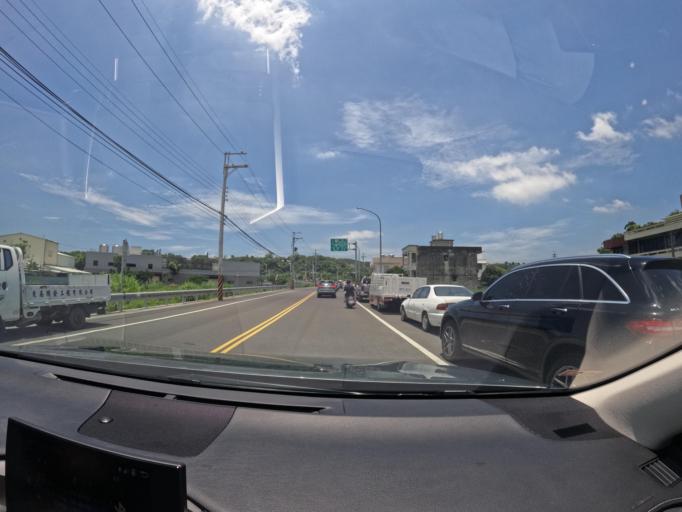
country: TW
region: Taiwan
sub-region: Hsinchu
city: Hsinchu
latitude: 24.6736
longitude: 120.9511
